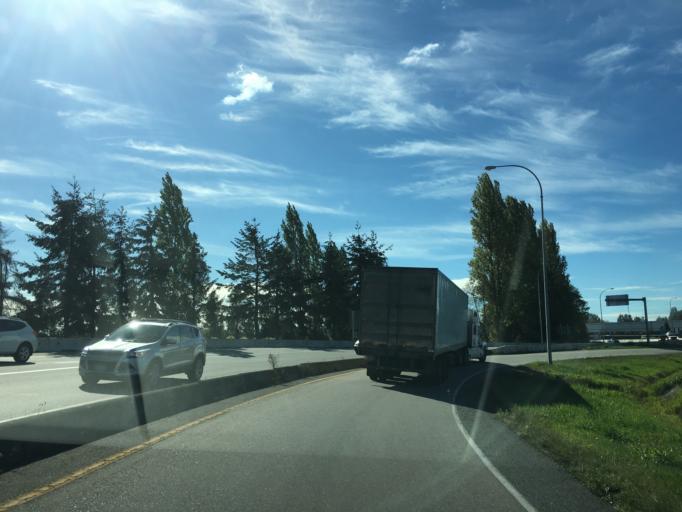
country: CA
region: British Columbia
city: Ladner
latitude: 49.1327
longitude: -123.0847
